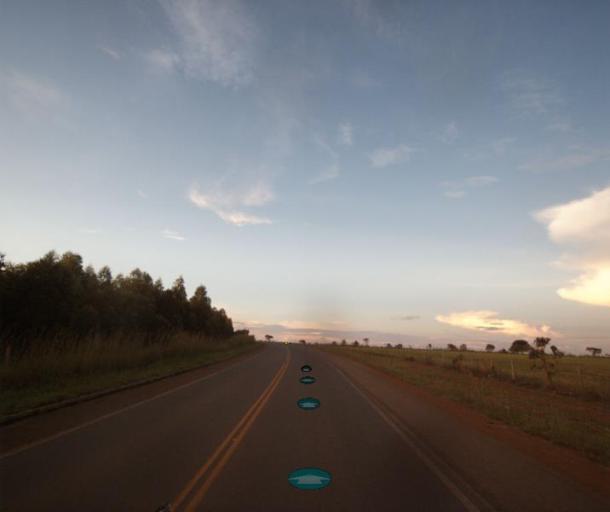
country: BR
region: Goias
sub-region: Pirenopolis
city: Pirenopolis
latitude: -16.0201
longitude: -48.8378
